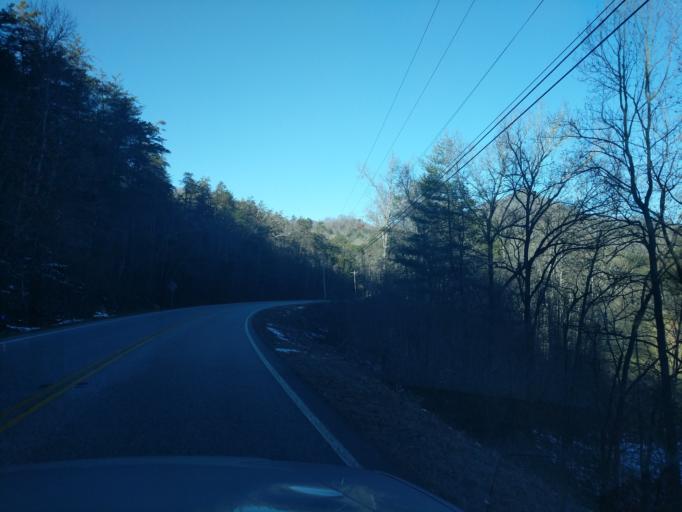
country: US
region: Georgia
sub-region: Towns County
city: Hiawassee
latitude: 34.9268
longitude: -83.6692
